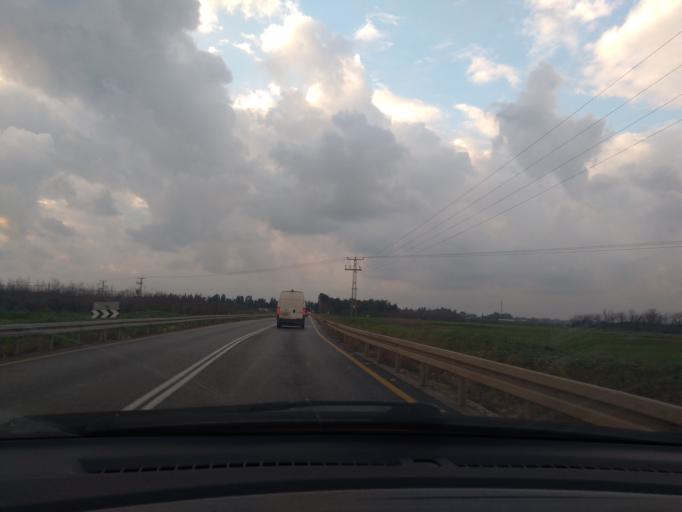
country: IL
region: Central District
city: Elyakhin
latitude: 32.3747
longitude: 34.9031
